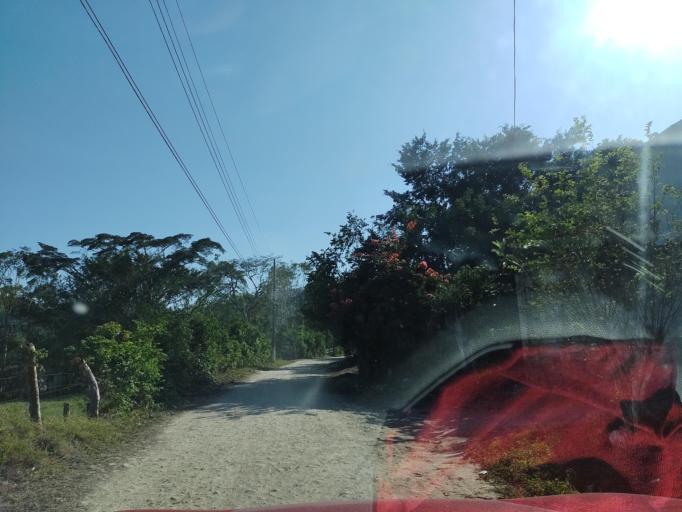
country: MX
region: Veracruz
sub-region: Papantla
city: Polutla
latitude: 20.4946
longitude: -97.1789
